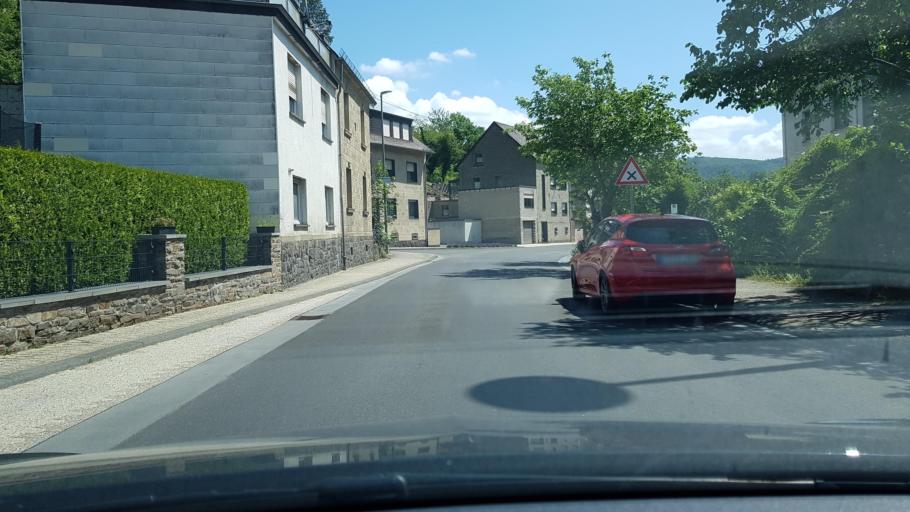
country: DE
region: Rheinland-Pfalz
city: Rieden
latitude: 50.3945
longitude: 7.1697
